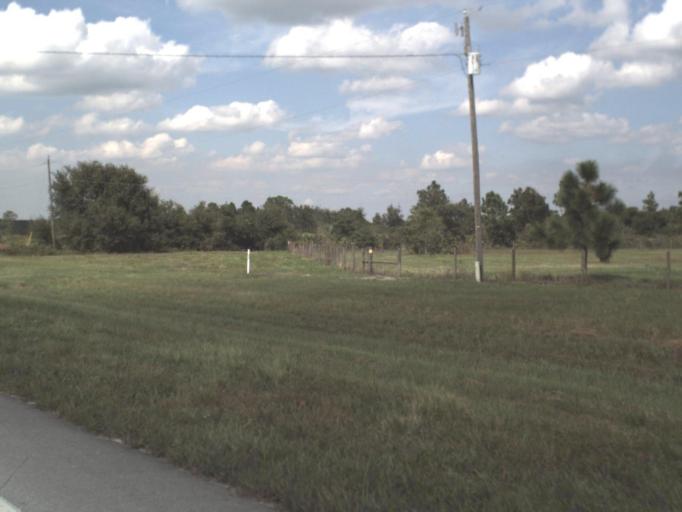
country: US
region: Florida
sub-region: Indian River County
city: Fellsmere
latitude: 27.6397
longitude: -80.8732
